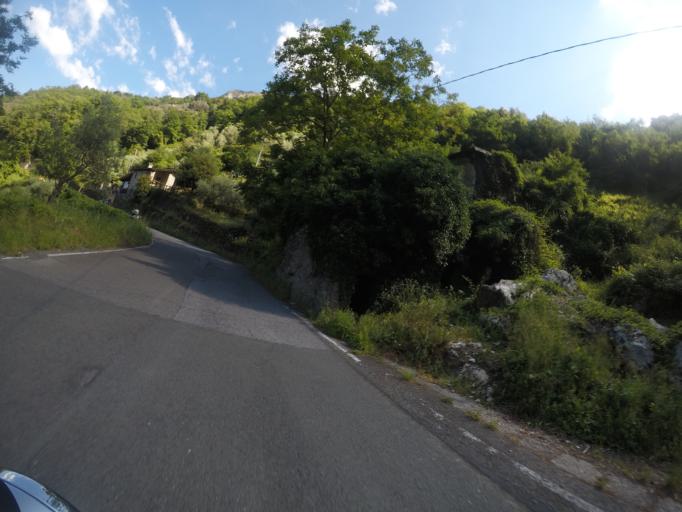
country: IT
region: Tuscany
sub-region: Provincia di Massa-Carrara
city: Montignoso
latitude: 44.0524
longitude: 10.1913
